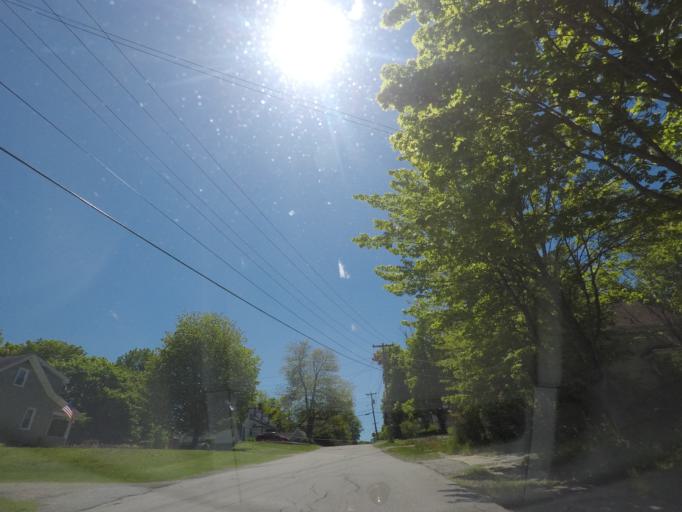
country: US
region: Maine
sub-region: Kennebec County
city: Gardiner
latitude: 44.2259
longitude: -69.7799
